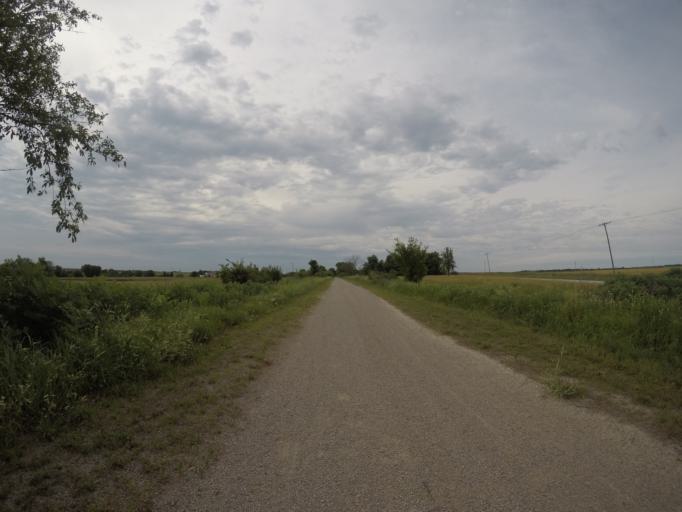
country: US
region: Kansas
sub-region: Franklin County
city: Ottawa
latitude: 38.4504
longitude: -95.2669
